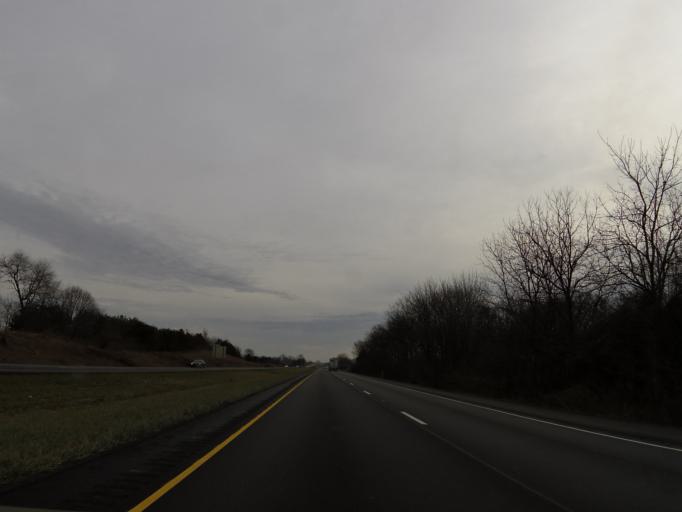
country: US
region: Indiana
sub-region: Montgomery County
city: Crawfordsville
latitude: 40.0995
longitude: -87.0448
